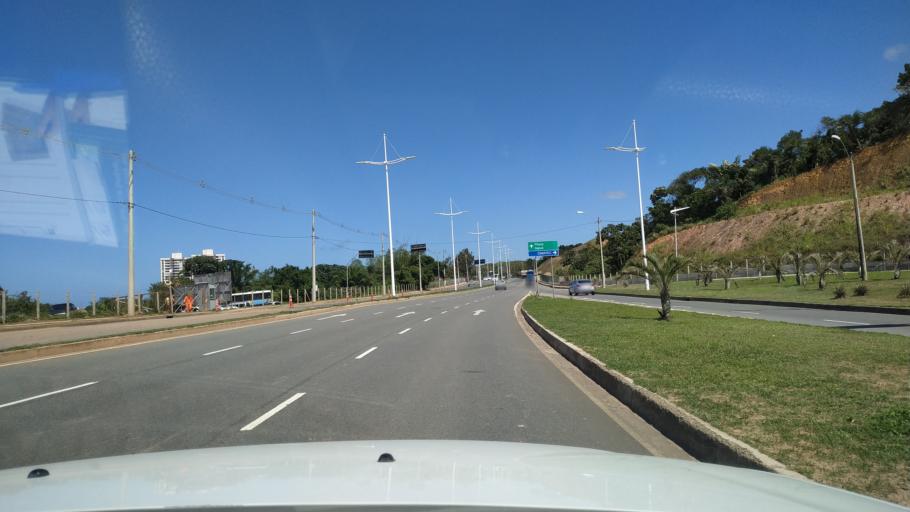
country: BR
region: Bahia
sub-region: Lauro De Freitas
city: Lauro de Freitas
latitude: -12.9312
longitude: -38.3821
